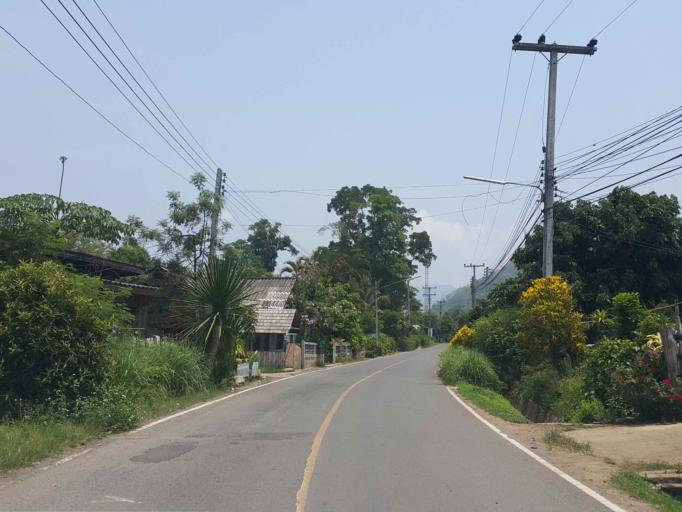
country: TH
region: Chiang Mai
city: Mae Taeng
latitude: 19.1705
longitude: 98.8574
